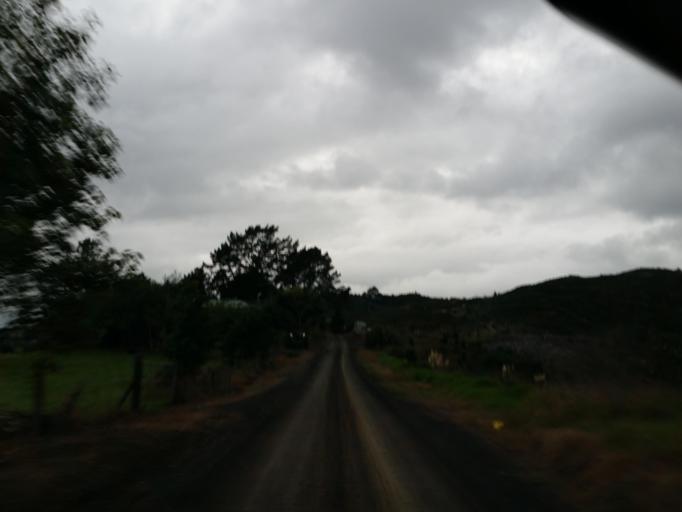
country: NZ
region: Northland
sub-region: Whangarei
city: Maungatapere
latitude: -35.8096
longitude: 174.0618
